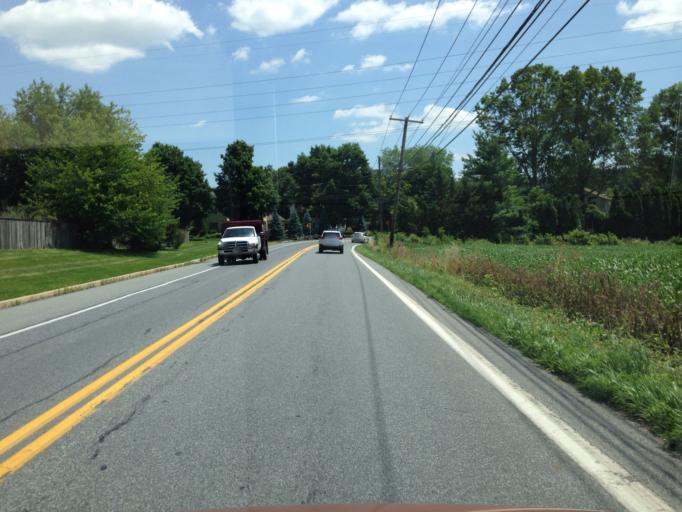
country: US
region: Pennsylvania
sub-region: Lancaster County
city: East Petersburg
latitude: 40.1004
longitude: -76.3296
